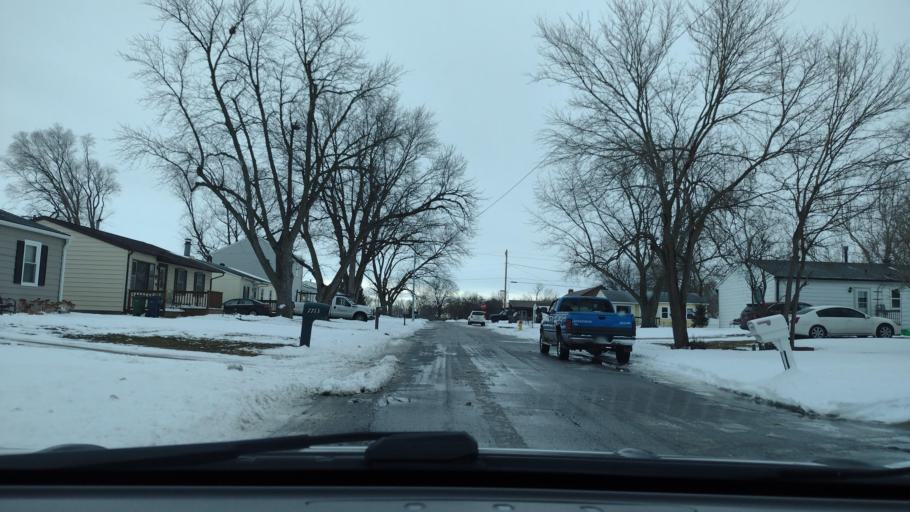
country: US
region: Nebraska
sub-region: Sarpy County
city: La Vista
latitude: 41.1808
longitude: -95.9726
